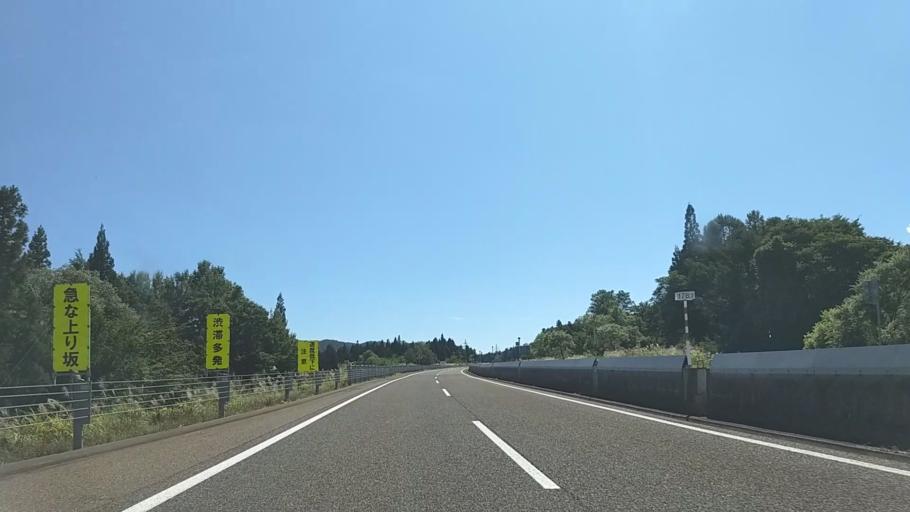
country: JP
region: Niigata
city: Arai
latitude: 36.9196
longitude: 138.2157
